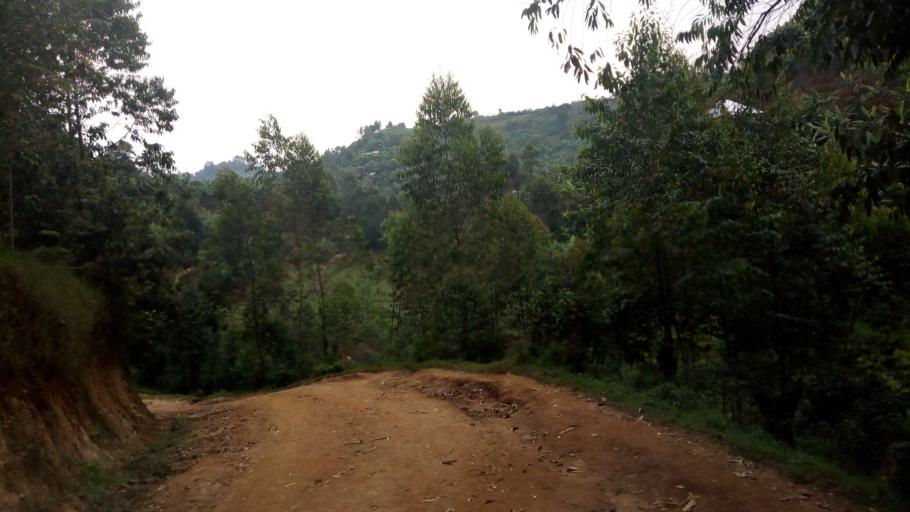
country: UG
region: Western Region
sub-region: Kisoro District
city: Kisoro
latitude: -1.2511
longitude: 29.6265
